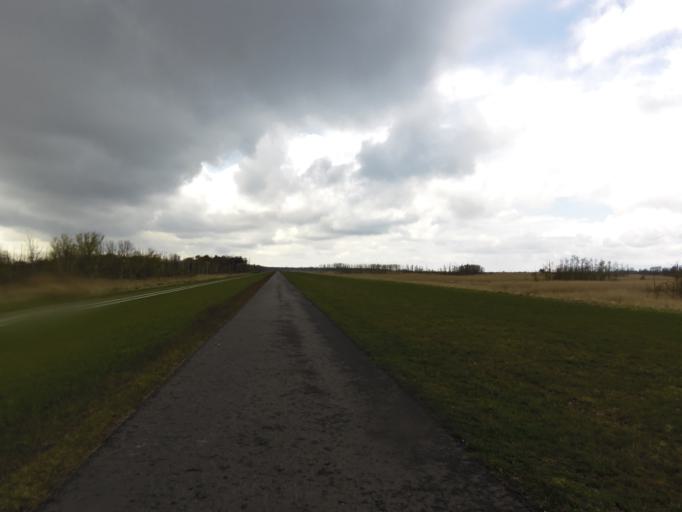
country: DE
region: Mecklenburg-Vorpommern
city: Barth
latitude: 54.4324
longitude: 12.8321
